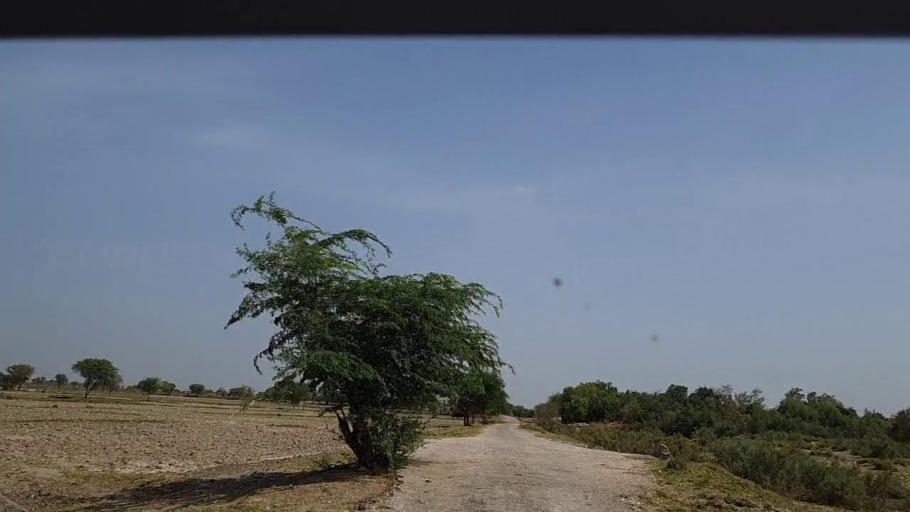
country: PK
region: Sindh
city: Phulji
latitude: 26.9469
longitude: 67.7163
